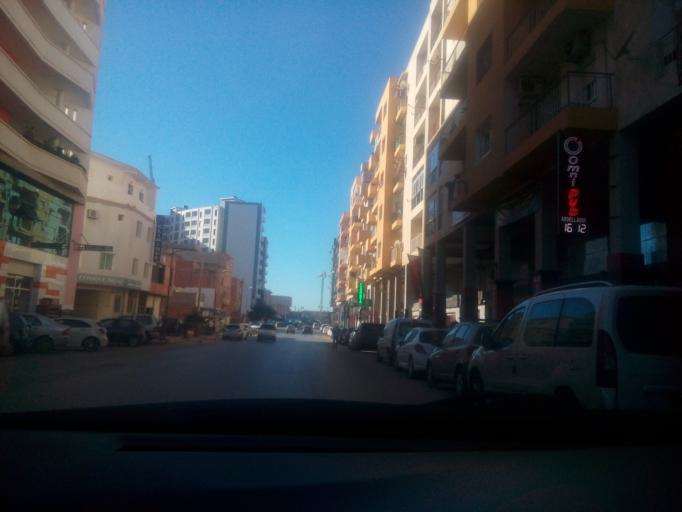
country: DZ
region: Oran
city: Bir el Djir
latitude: 35.7215
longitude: -0.5808
